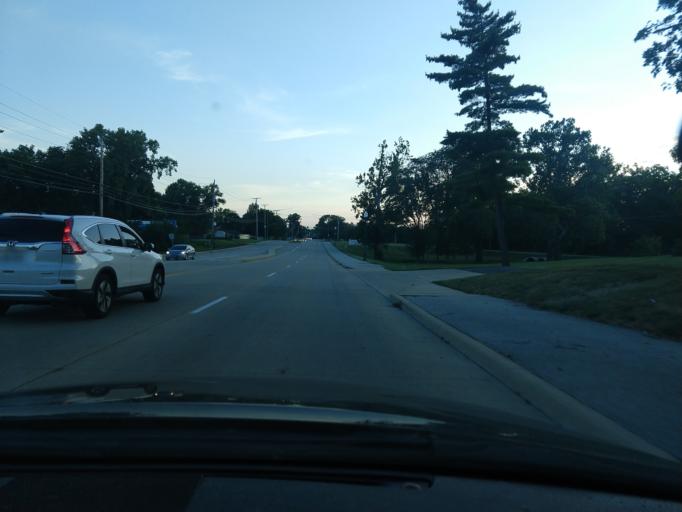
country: US
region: Indiana
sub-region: Hamilton County
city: Fishers
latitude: 39.9331
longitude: -86.0585
